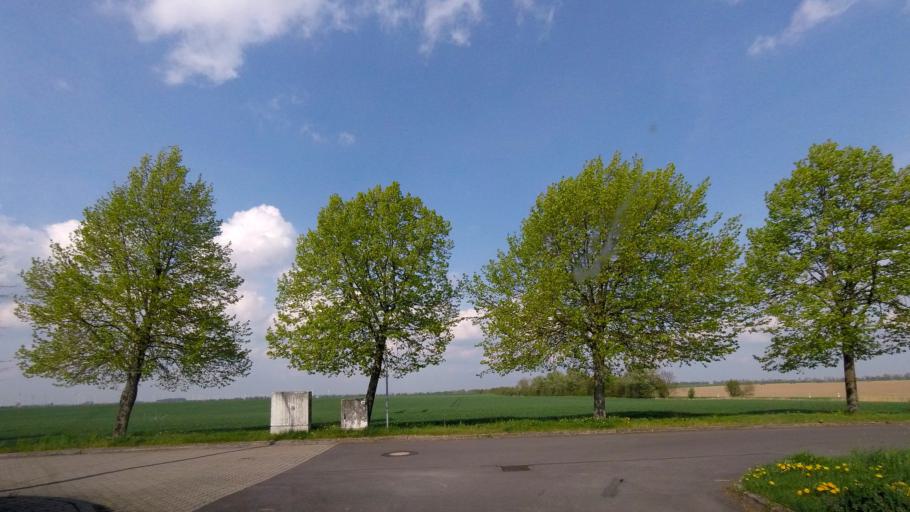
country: DE
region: Saxony-Anhalt
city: Seyda
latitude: 51.9586
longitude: 12.8952
